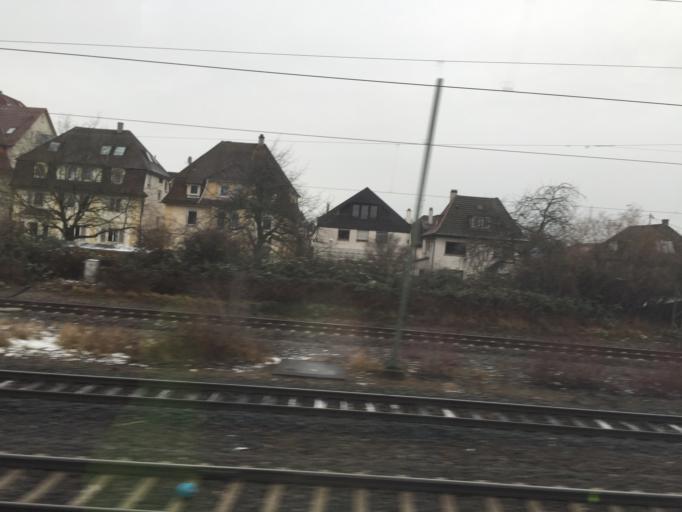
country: DE
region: Baden-Wuerttemberg
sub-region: Regierungsbezirk Stuttgart
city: Kornwestheim
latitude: 48.8638
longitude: 9.1805
